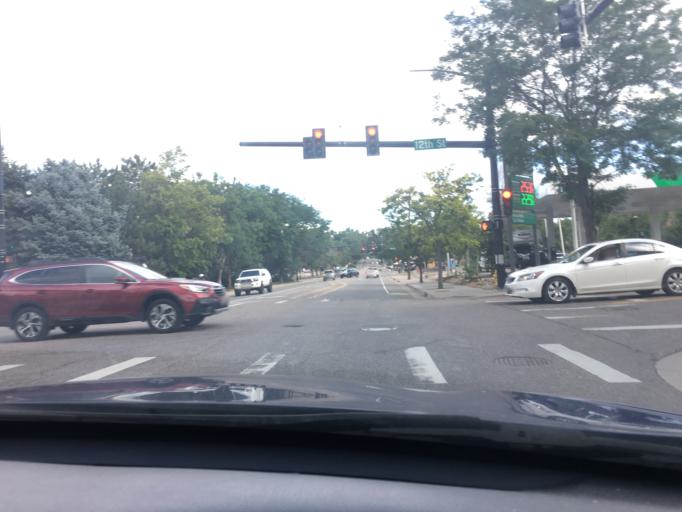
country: US
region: Colorado
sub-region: Jefferson County
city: Golden
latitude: 39.7567
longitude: -105.2194
